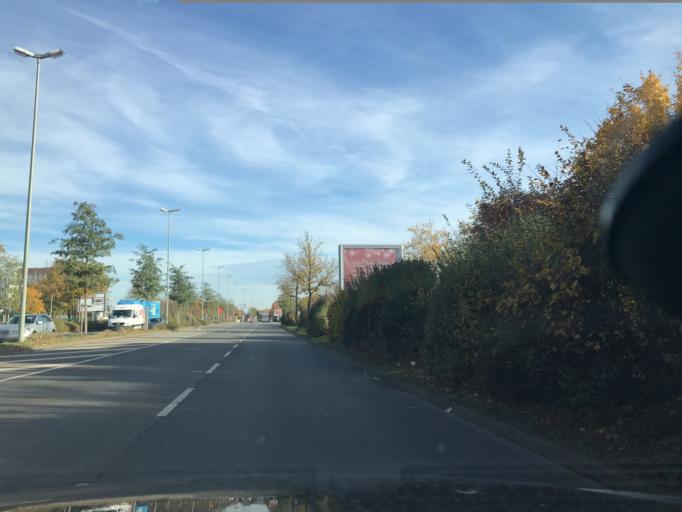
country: DE
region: North Rhine-Westphalia
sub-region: Regierungsbezirk Dusseldorf
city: Krefeld
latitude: 51.3172
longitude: 6.5784
